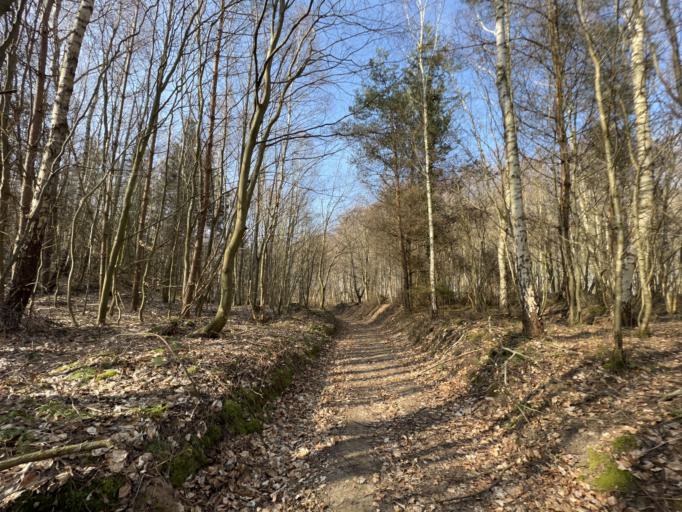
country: DE
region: Mecklenburg-Vorpommern
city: Sagard
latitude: 54.4804
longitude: 13.5550
